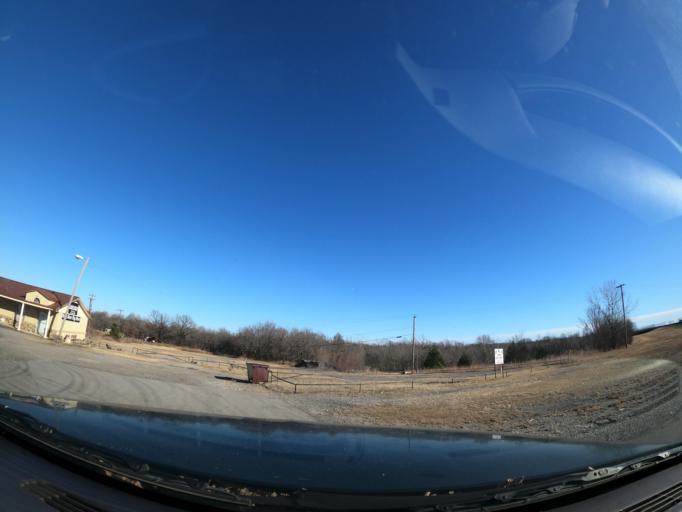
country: US
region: Oklahoma
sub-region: McIntosh County
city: Eufaula
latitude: 35.2712
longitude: -95.5853
